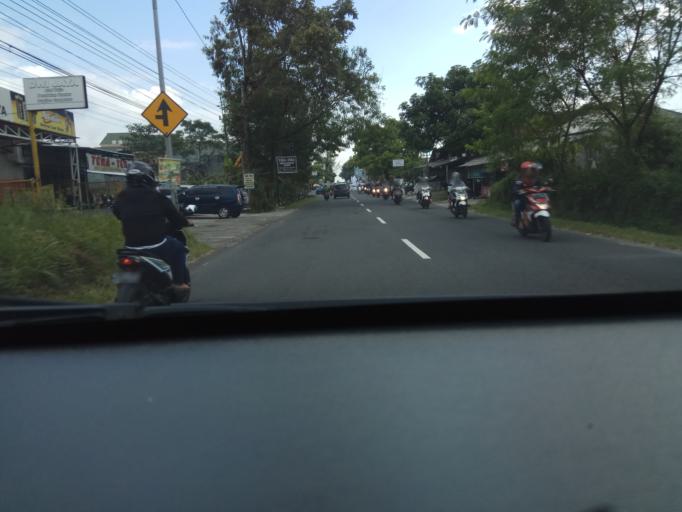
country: ID
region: Daerah Istimewa Yogyakarta
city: Melati
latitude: -7.7116
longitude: 110.4085
